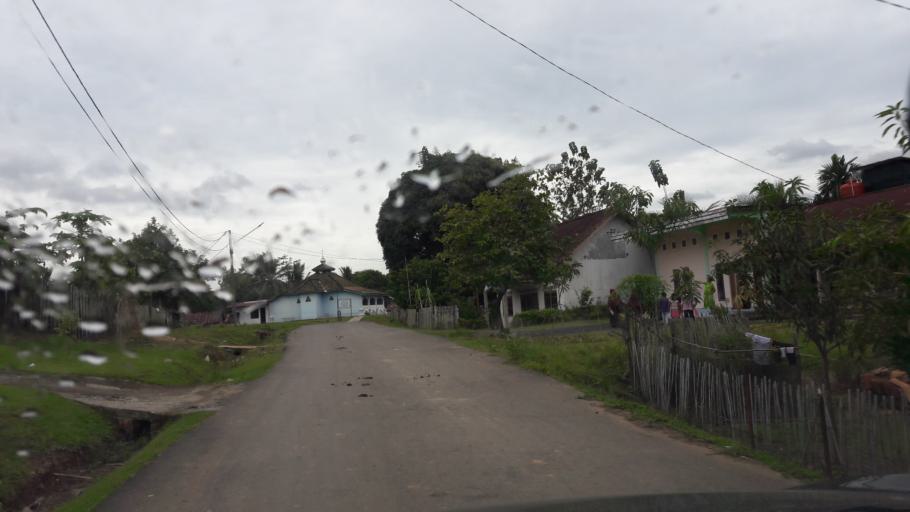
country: ID
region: South Sumatra
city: Gunungmenang
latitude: -3.1848
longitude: 103.7898
